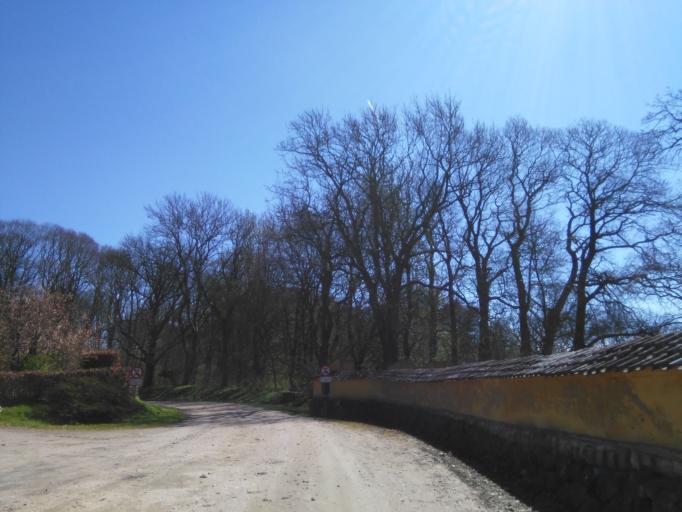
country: DK
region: Central Jutland
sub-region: Hedensted Kommune
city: Juelsminde
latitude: 55.7470
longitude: 10.0275
